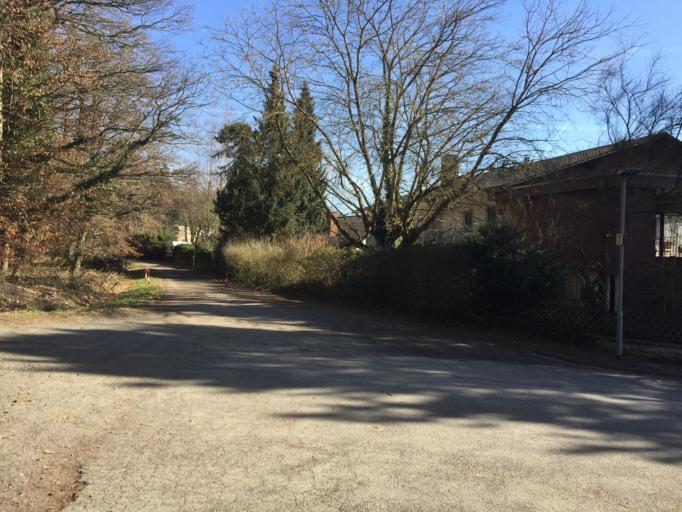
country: DE
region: Hesse
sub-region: Regierungsbezirk Giessen
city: Langgons
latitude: 50.5380
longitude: 8.6859
